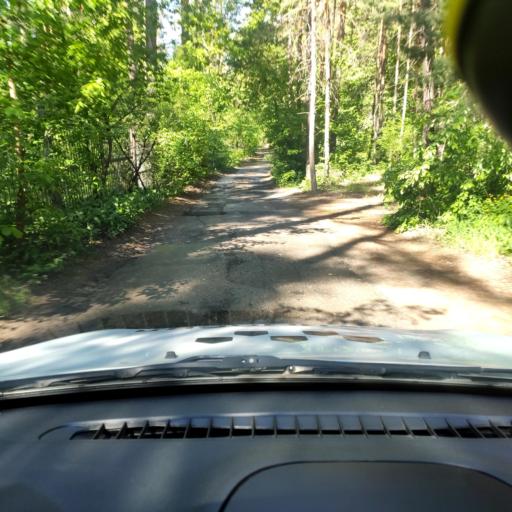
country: RU
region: Samara
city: Tol'yatti
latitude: 53.4686
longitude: 49.3887
